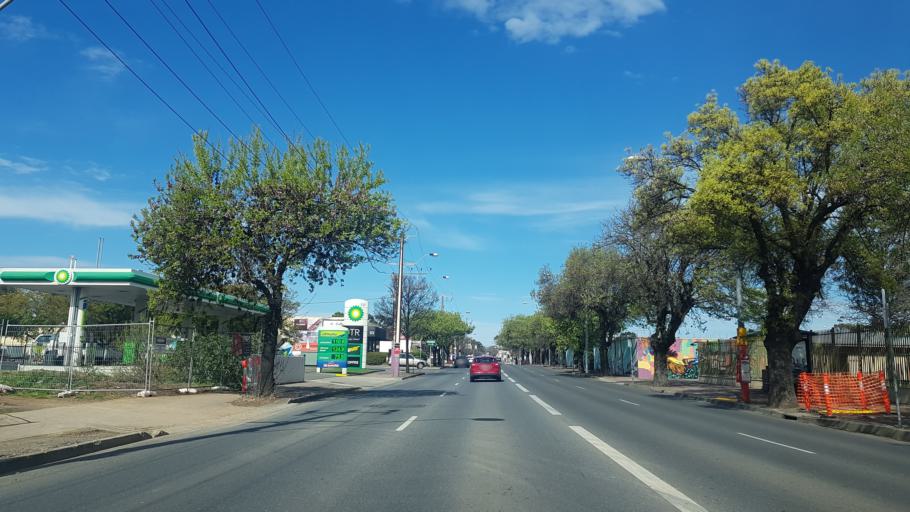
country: AU
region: South Australia
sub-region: Unley
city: Wayville
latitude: -34.9460
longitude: 138.5893
